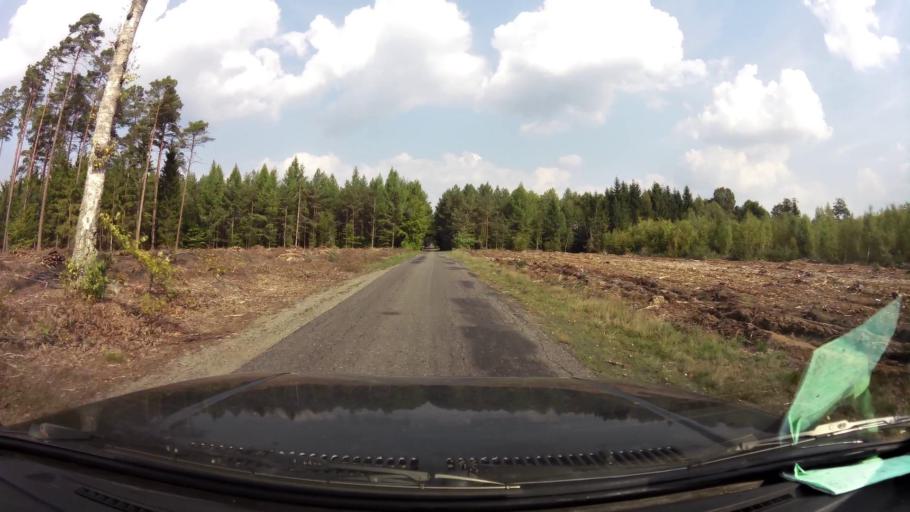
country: PL
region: West Pomeranian Voivodeship
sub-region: Powiat koszalinski
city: Bobolice
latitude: 54.0901
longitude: 16.4843
